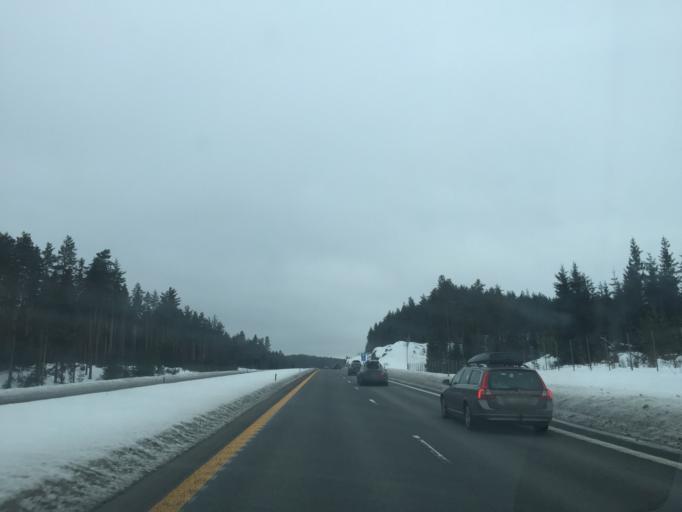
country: NO
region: Hedmark
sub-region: Stange
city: Stange
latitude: 60.6428
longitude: 11.2959
